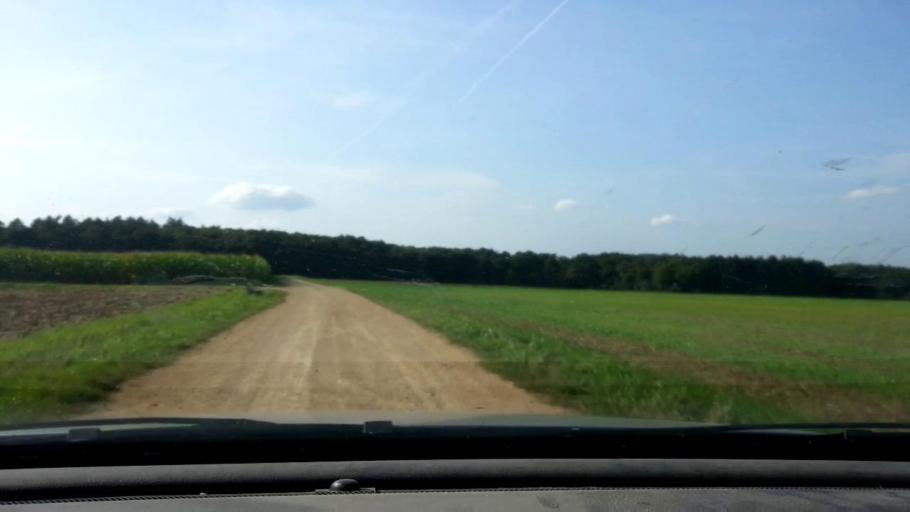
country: DE
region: Bavaria
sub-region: Upper Franconia
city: Zapfendorf
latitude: 49.9967
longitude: 10.9309
